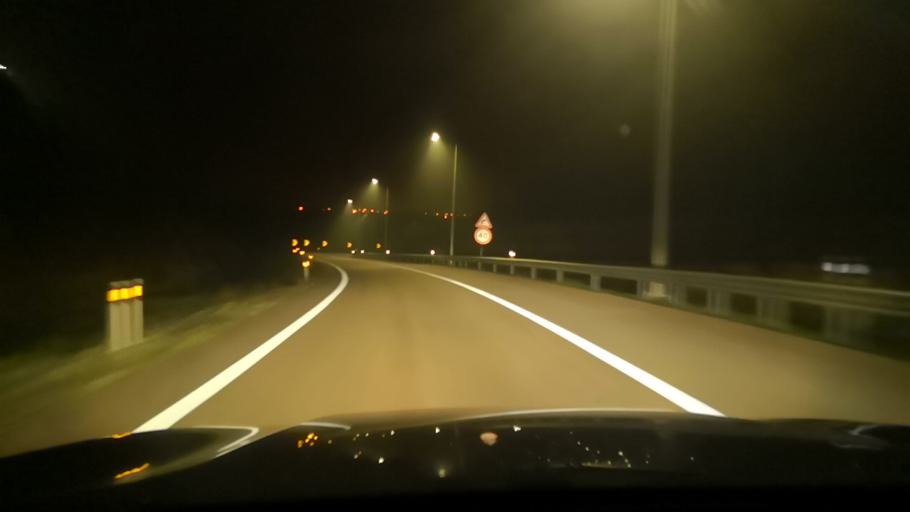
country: PT
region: Evora
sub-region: Vendas Novas
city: Vendas Novas
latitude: 38.6054
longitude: -8.6497
